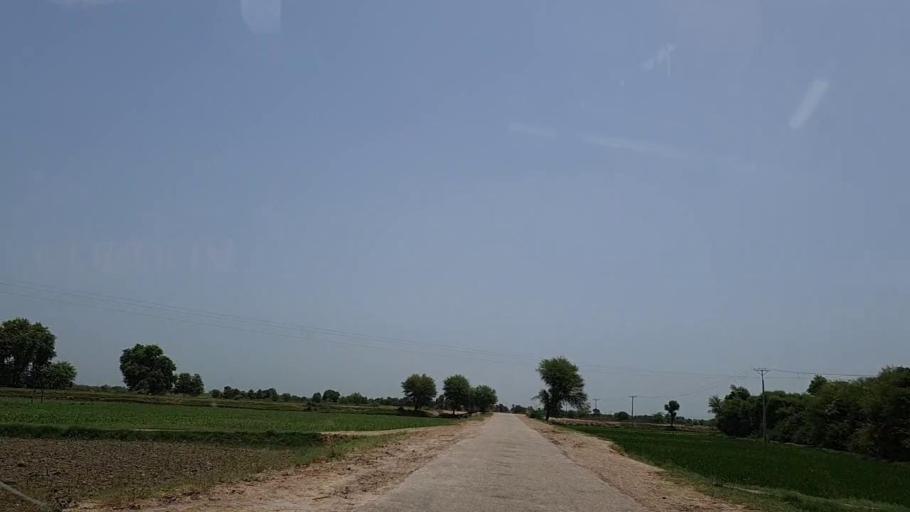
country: PK
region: Sindh
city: Tharu Shah
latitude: 26.9573
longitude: 68.0733
